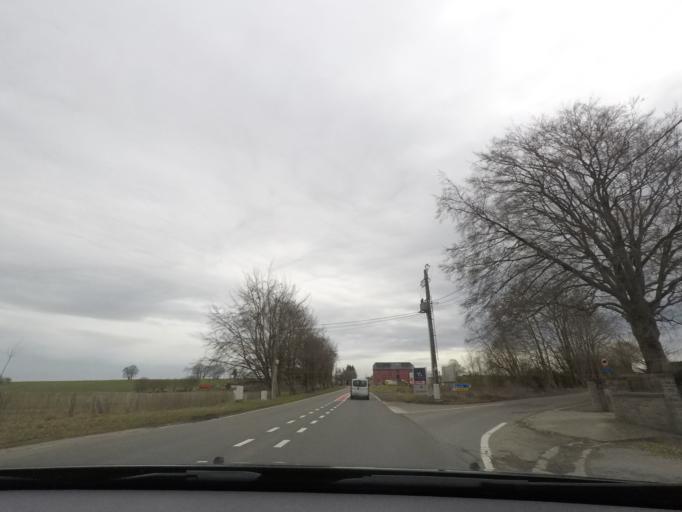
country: BE
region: Wallonia
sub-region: Province du Luxembourg
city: Bastogne
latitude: 49.9930
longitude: 5.7357
